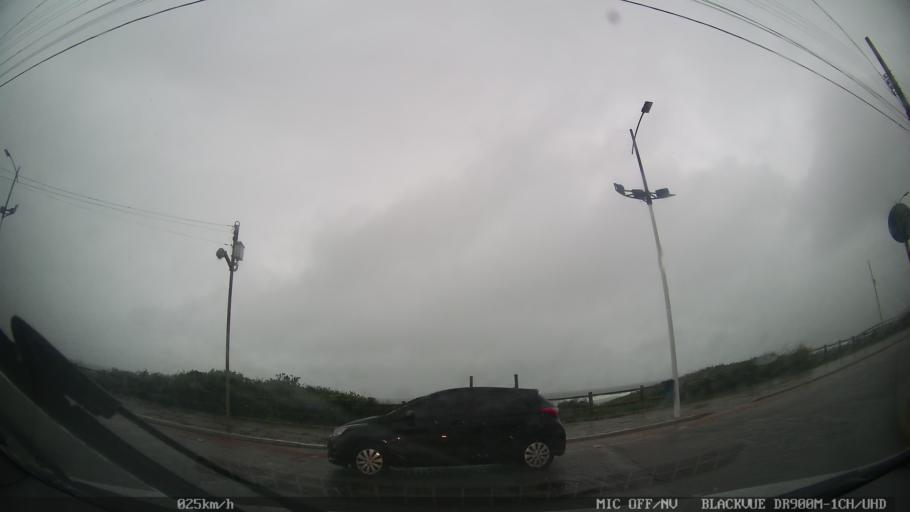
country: BR
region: Santa Catarina
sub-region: Balneario Camboriu
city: Balneario Camboriu
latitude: -26.9456
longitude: -48.6290
